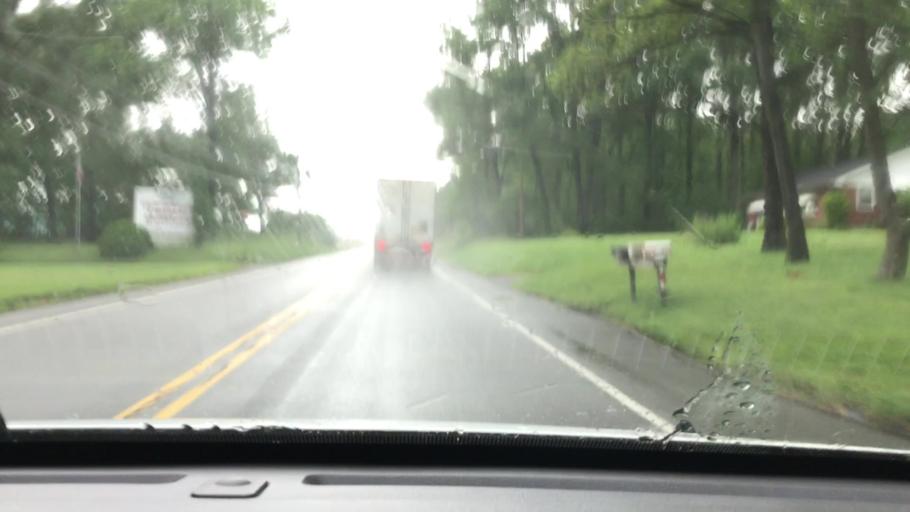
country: US
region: Pennsylvania
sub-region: Clearfield County
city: Shiloh
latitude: 40.9941
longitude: -78.3118
